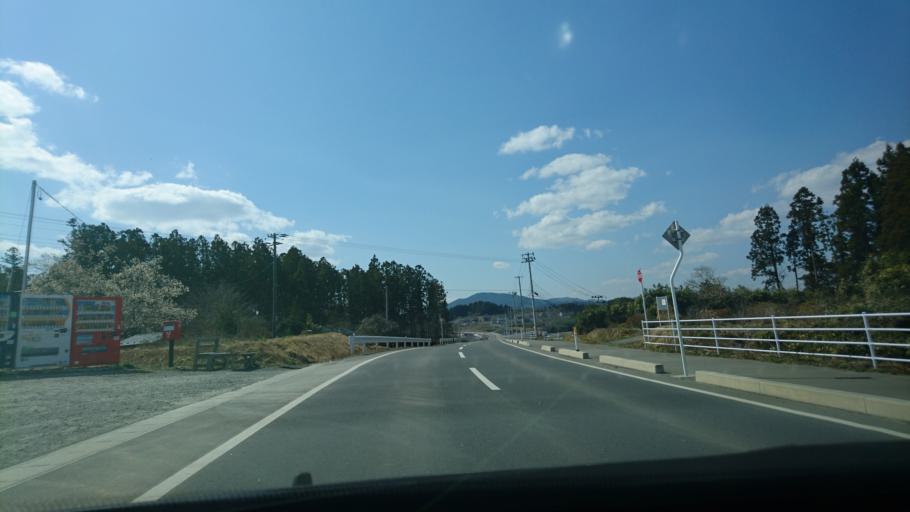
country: JP
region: Miyagi
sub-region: Oshika Gun
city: Onagawa Cho
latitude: 38.6432
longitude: 141.4735
